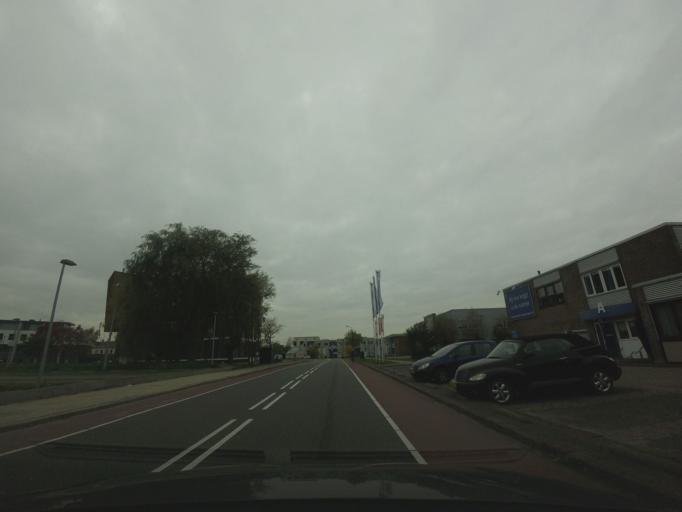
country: NL
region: North Holland
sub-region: Gemeente Langedijk
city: Broek op Langedijk
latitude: 52.6675
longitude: 4.8209
